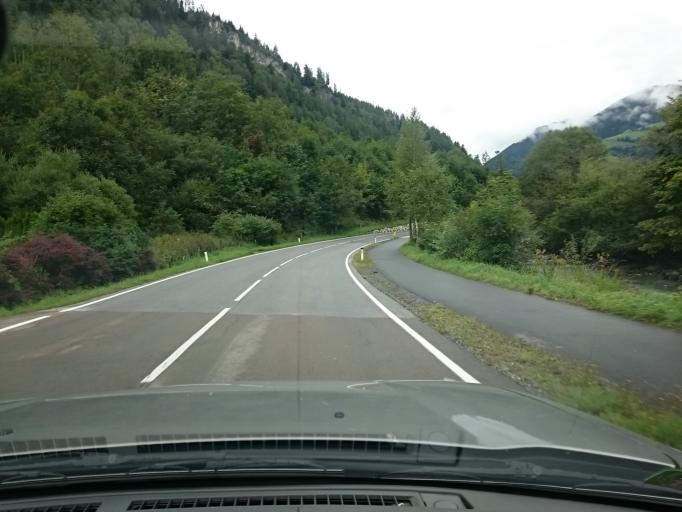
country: AT
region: Salzburg
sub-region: Politischer Bezirk Zell am See
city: Bruck an der Grossglocknerstrasse
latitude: 47.2658
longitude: 12.8243
